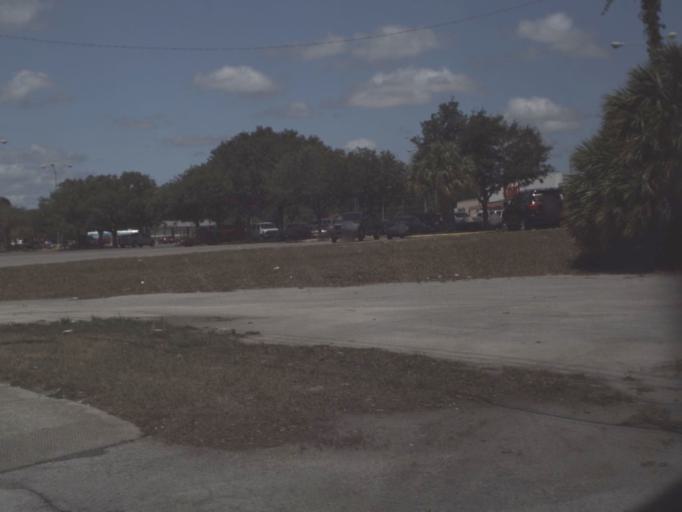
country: US
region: Florida
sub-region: Marion County
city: Ocala
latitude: 29.1996
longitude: -82.0839
